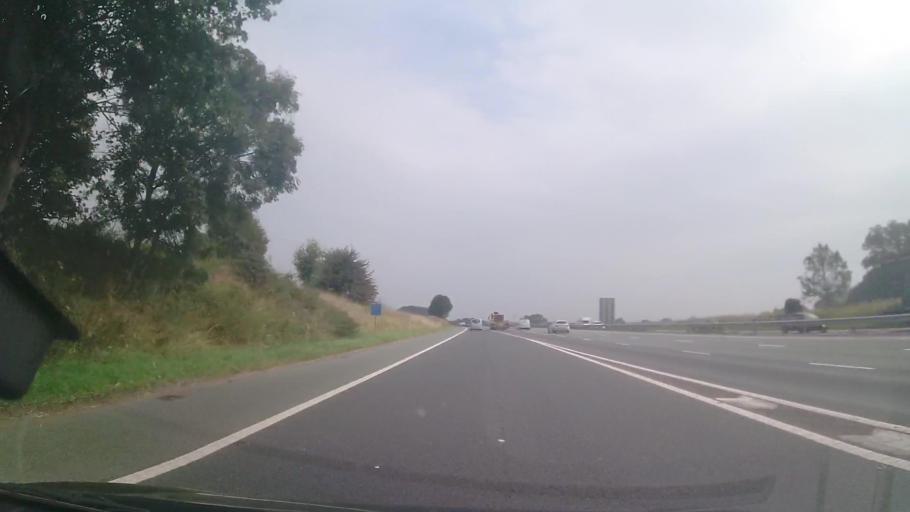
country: GB
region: England
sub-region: Warrington
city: Stretton
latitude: 53.3361
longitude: -2.5660
